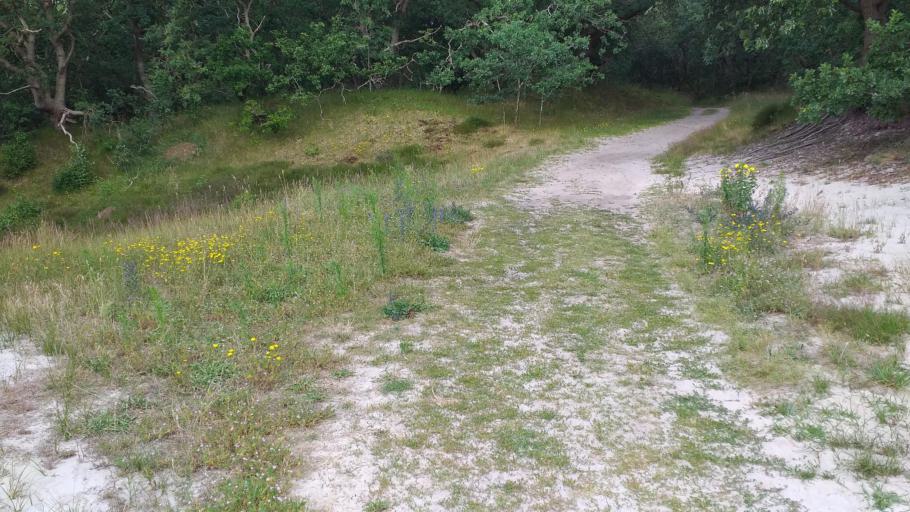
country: NL
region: North Holland
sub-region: Gemeente Bergen
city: Egmond aan Zee
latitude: 52.6706
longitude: 4.6601
